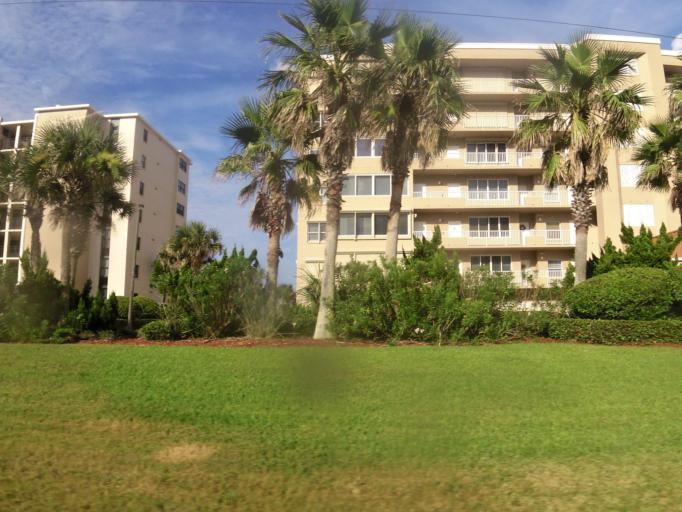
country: US
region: Florida
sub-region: Volusia County
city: Ponce Inlet
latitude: 29.0936
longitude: -80.9333
